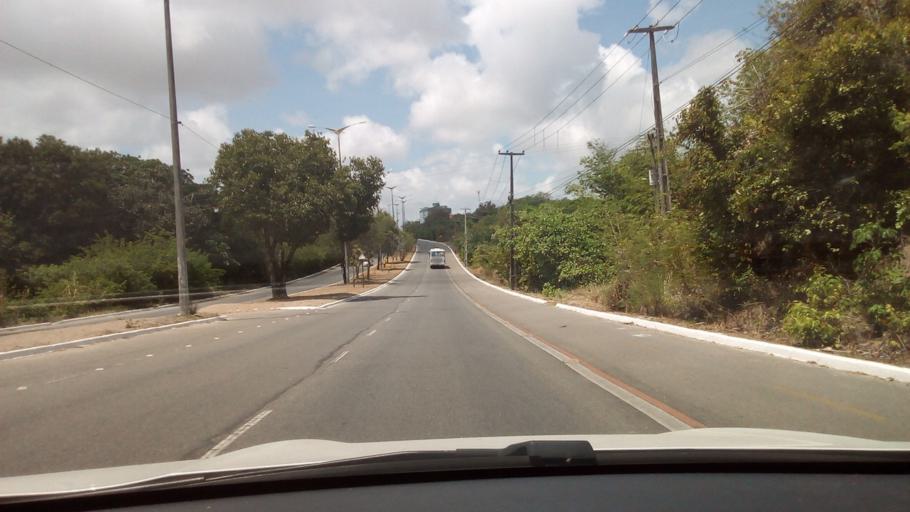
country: BR
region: Paraiba
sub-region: Joao Pessoa
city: Joao Pessoa
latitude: -7.1604
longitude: -34.8127
